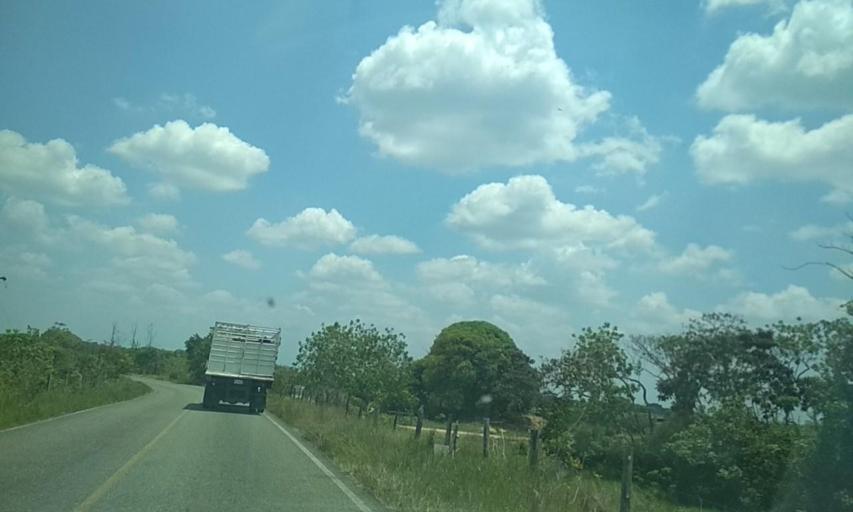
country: MX
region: Tabasco
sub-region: Huimanguillo
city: Francisco Rueda
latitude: 17.7694
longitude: -93.8017
